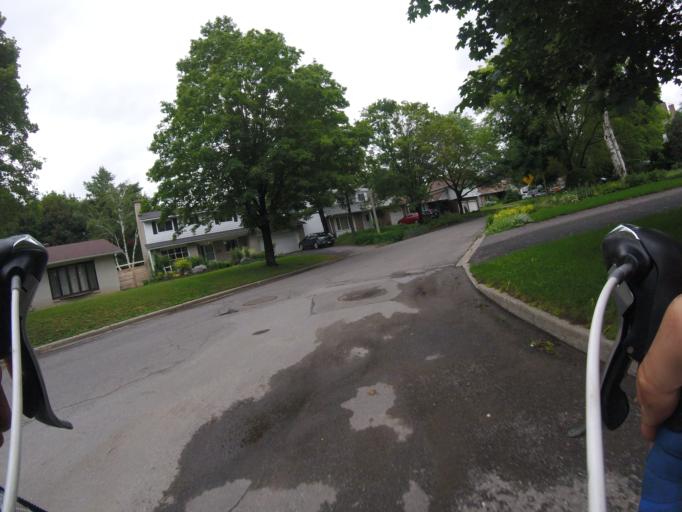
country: CA
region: Ontario
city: Bells Corners
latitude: 45.3698
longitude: -75.7881
